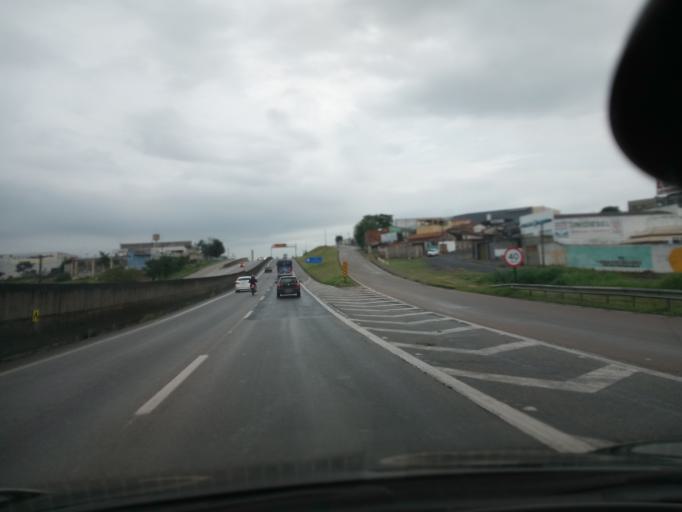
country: BR
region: Sao Paulo
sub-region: Campinas
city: Campinas
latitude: -22.9401
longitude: -47.0866
